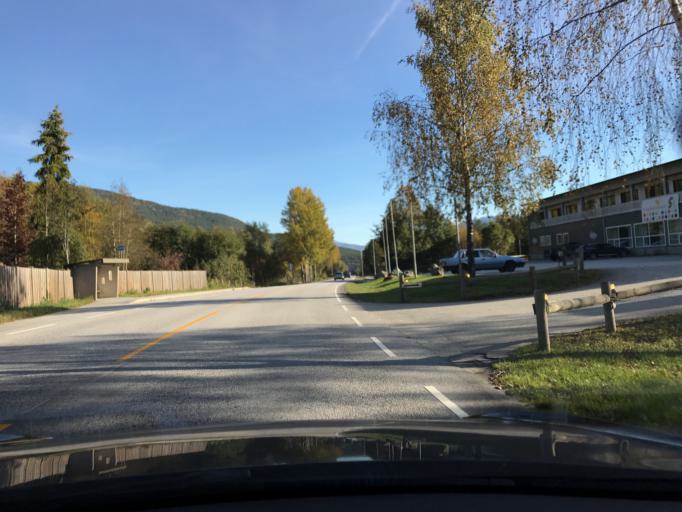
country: NO
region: Sogn og Fjordane
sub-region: Sogndal
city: Sogndalsfjora
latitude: 61.2056
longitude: 7.1999
